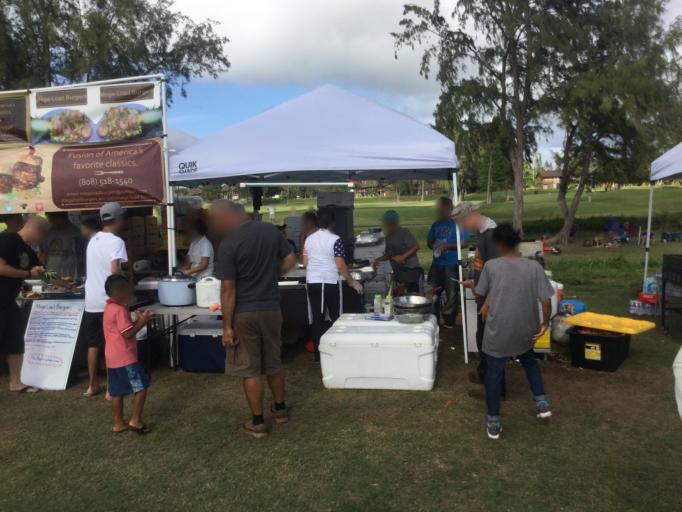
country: US
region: Hawaii
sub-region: Honolulu County
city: Kahuku
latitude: 21.6995
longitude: -157.9991
